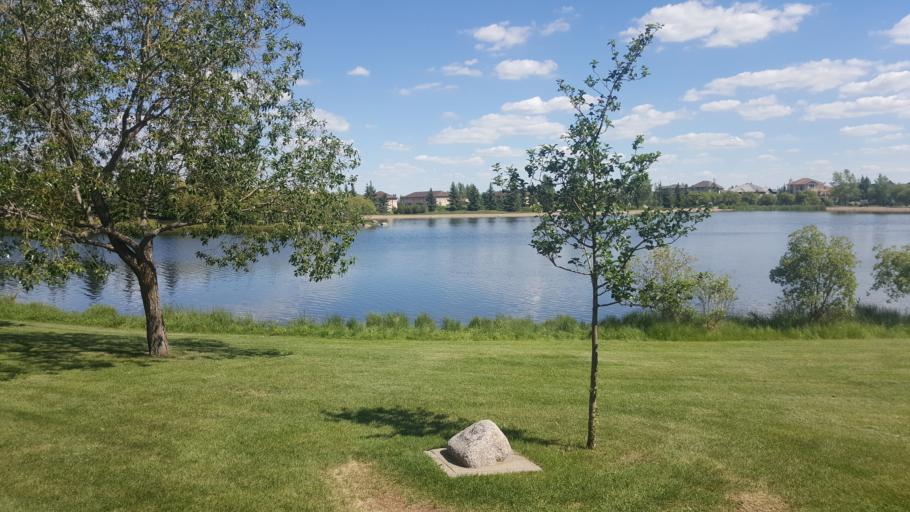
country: CA
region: Saskatchewan
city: Lloydminster
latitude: 53.2603
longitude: -110.0414
